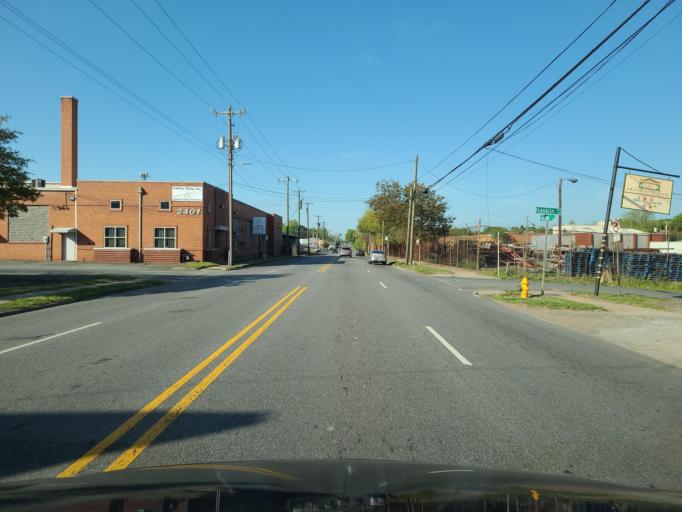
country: US
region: North Carolina
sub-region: Mecklenburg County
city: Charlotte
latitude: 35.2507
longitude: -80.8274
